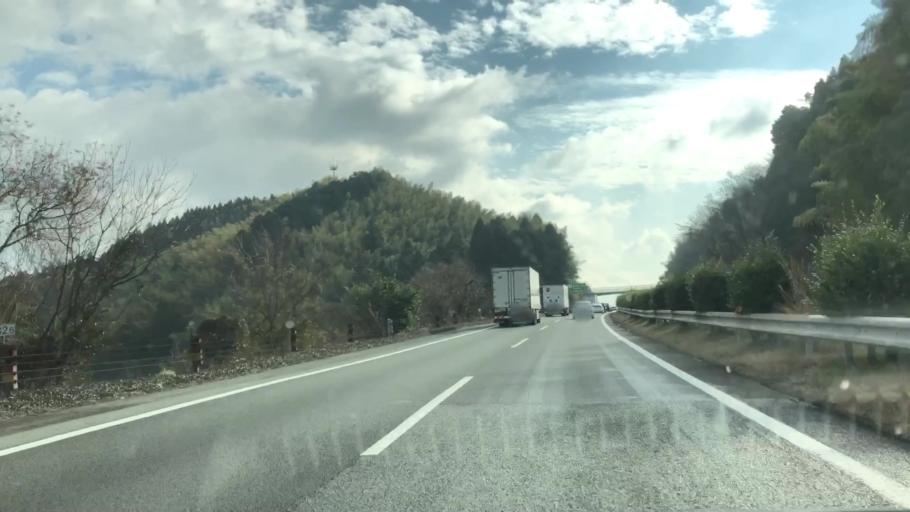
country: JP
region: Fukuoka
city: Setakamachi-takayanagi
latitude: 33.0927
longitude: 130.5384
